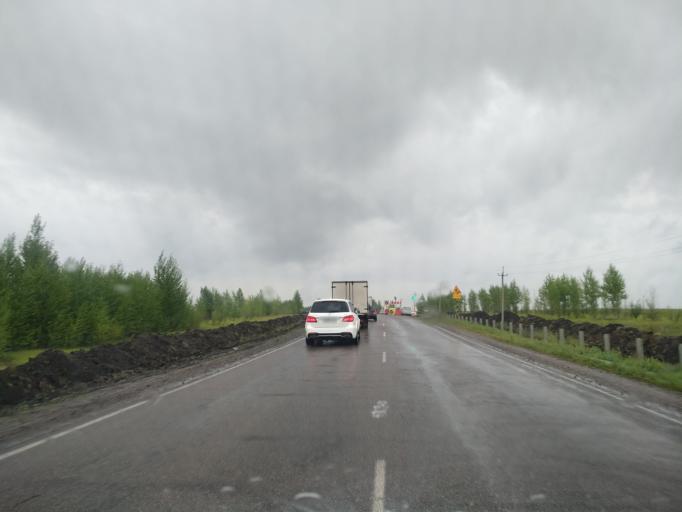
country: RU
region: Voronezj
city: Verkhnyaya Khava
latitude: 51.6743
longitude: 39.8257
